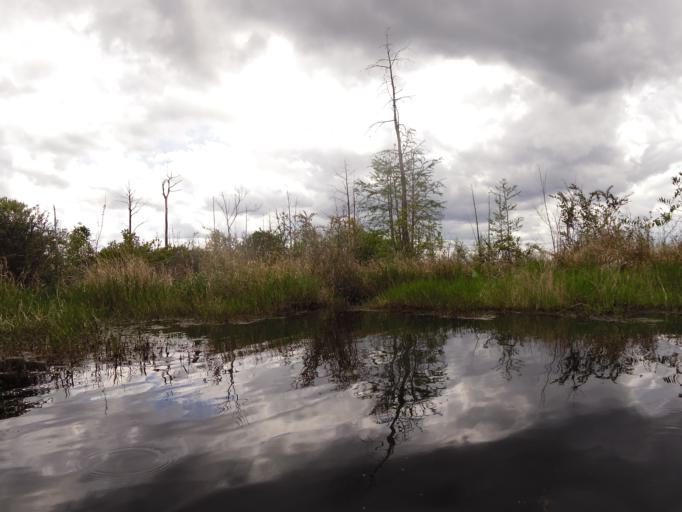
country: US
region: Georgia
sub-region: Charlton County
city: Folkston
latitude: 30.7356
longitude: -82.1603
